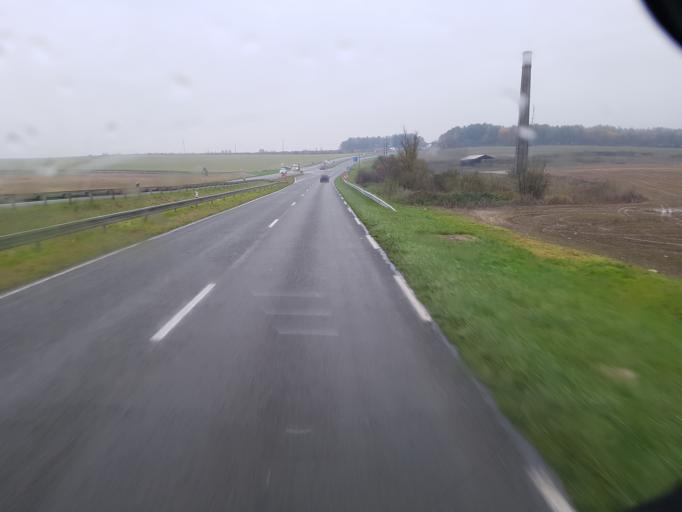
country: FR
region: Picardie
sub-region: Departement de l'Aisne
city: Gauchy
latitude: 49.8078
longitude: 3.2865
